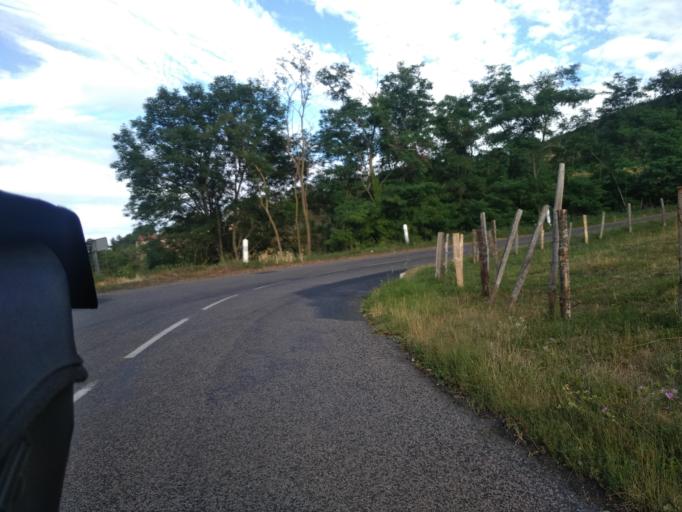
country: FR
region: Rhone-Alpes
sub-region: Departement du Rhone
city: Montrottier
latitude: 45.7865
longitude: 4.4951
